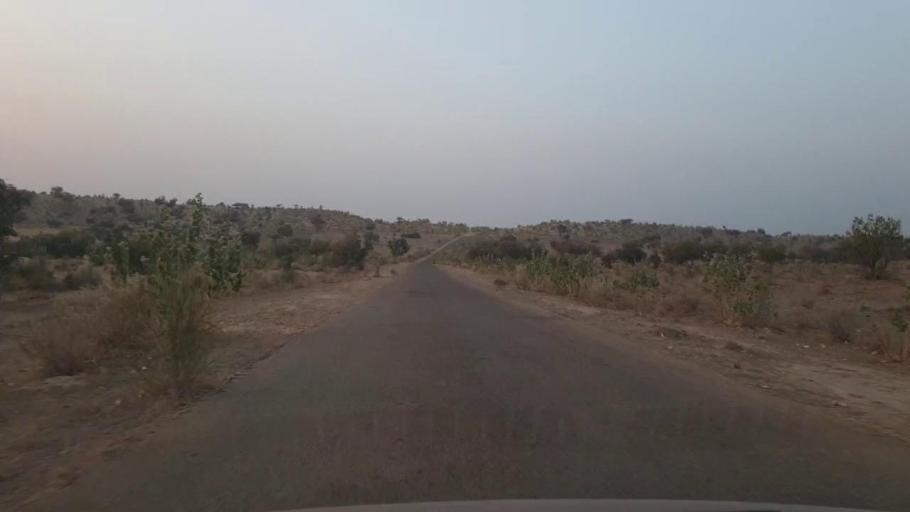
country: PK
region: Sindh
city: Umarkot
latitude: 25.3151
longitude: 70.0594
